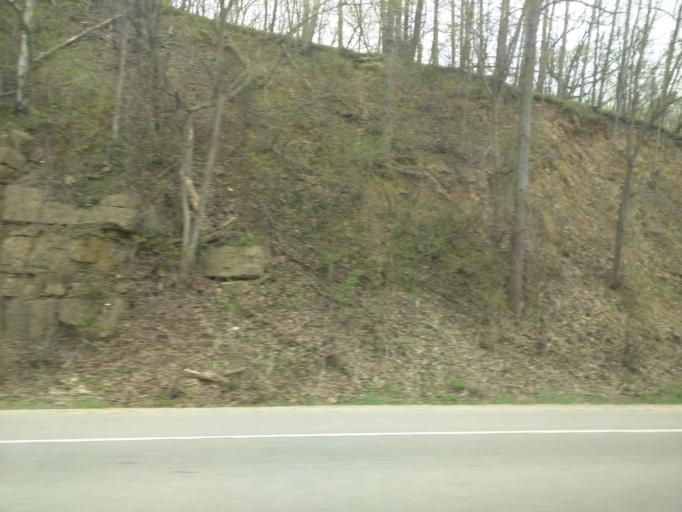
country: US
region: Minnesota
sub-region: Goodhue County
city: Red Wing
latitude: 44.5812
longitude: -92.3784
